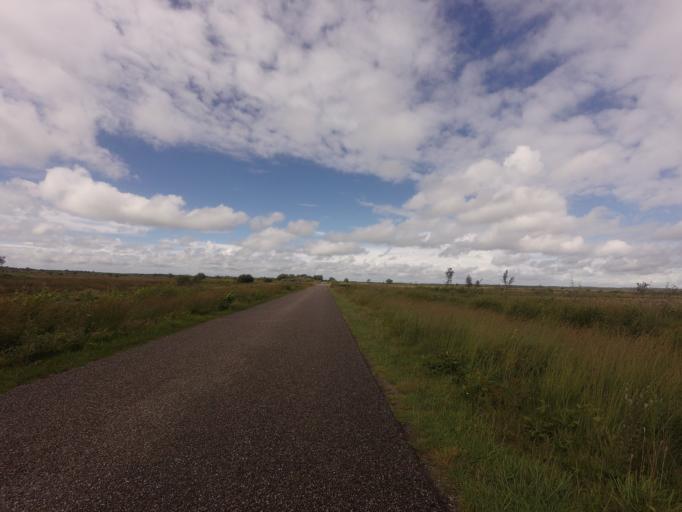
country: NL
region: Drenthe
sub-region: Gemeente Westerveld
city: Dwingeloo
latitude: 52.9971
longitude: 6.3768
